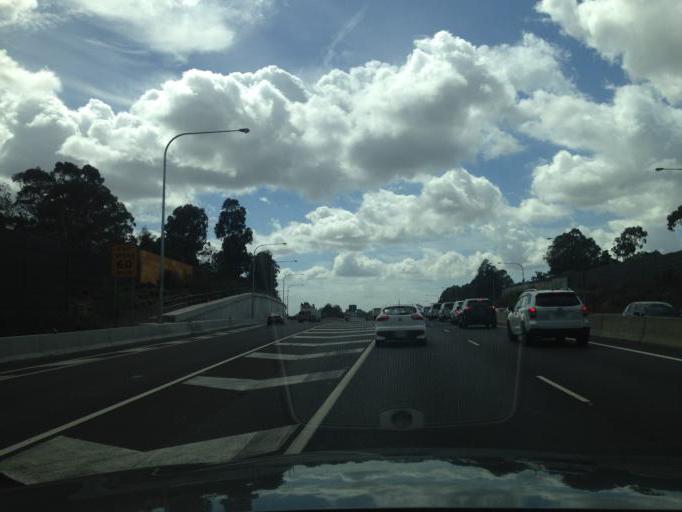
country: AU
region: New South Wales
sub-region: Canterbury
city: Roselands
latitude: -33.9436
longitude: 151.0720
